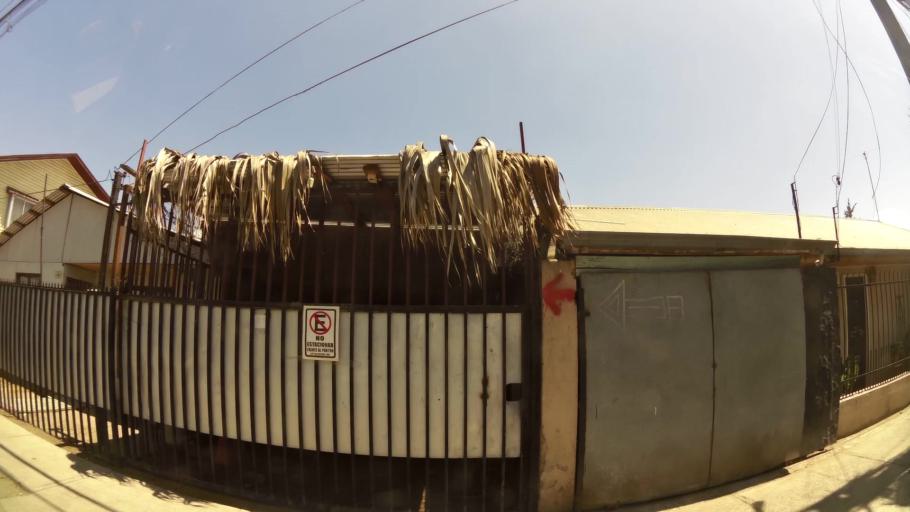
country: CL
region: Santiago Metropolitan
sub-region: Provincia de Talagante
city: Penaflor
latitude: -33.5681
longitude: -70.7909
